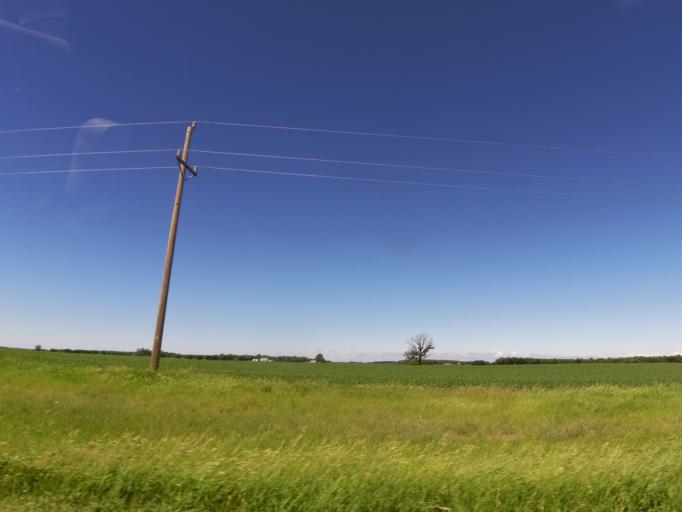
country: US
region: Minnesota
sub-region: Polk County
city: Fosston
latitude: 47.6347
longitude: -95.9830
